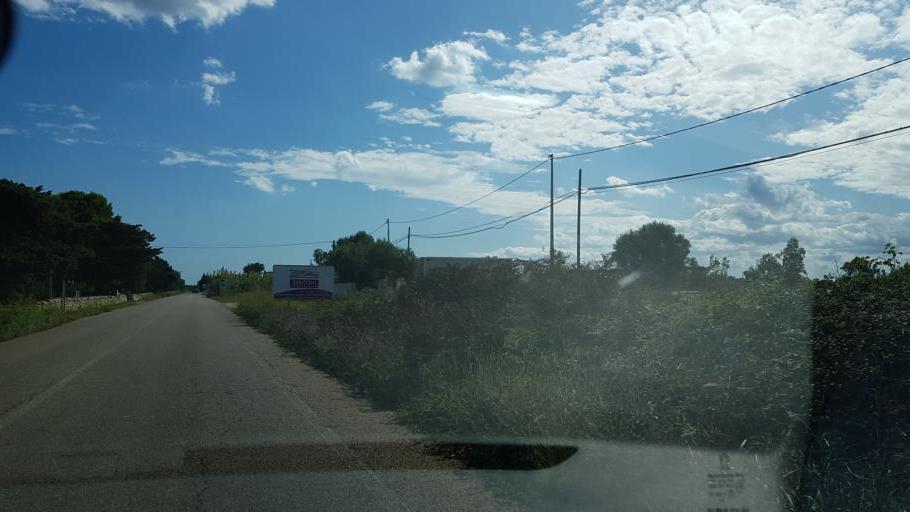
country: IT
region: Apulia
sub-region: Provincia di Lecce
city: Borgagne
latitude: 40.2647
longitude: 18.4323
